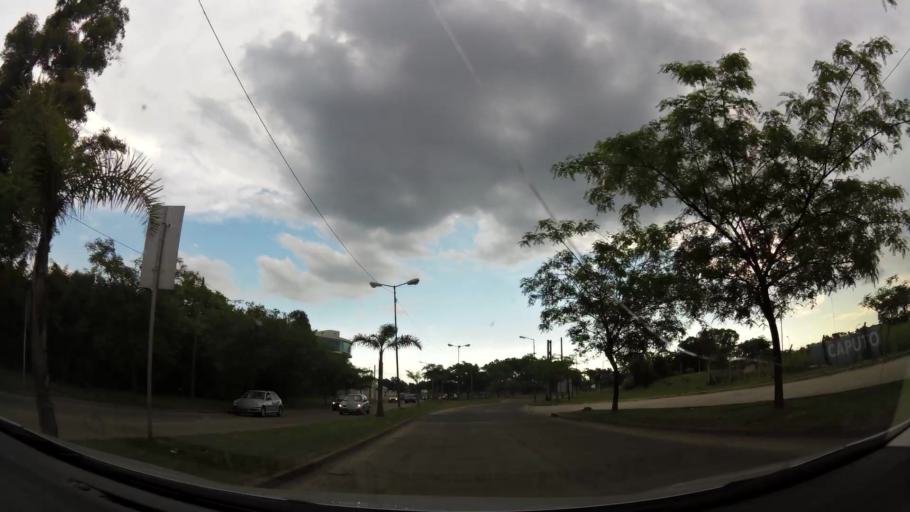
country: AR
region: Buenos Aires
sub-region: Partido de Tigre
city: Tigre
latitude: -34.4850
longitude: -58.5914
